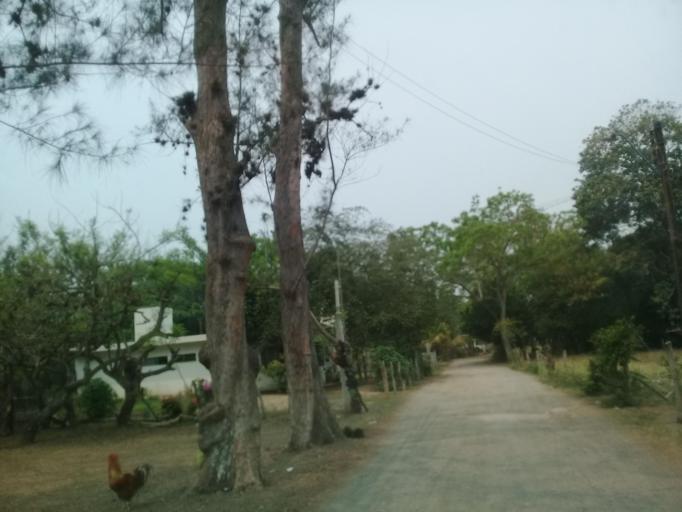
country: MX
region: Veracruz
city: Jamapa
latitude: 18.9520
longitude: -96.2043
